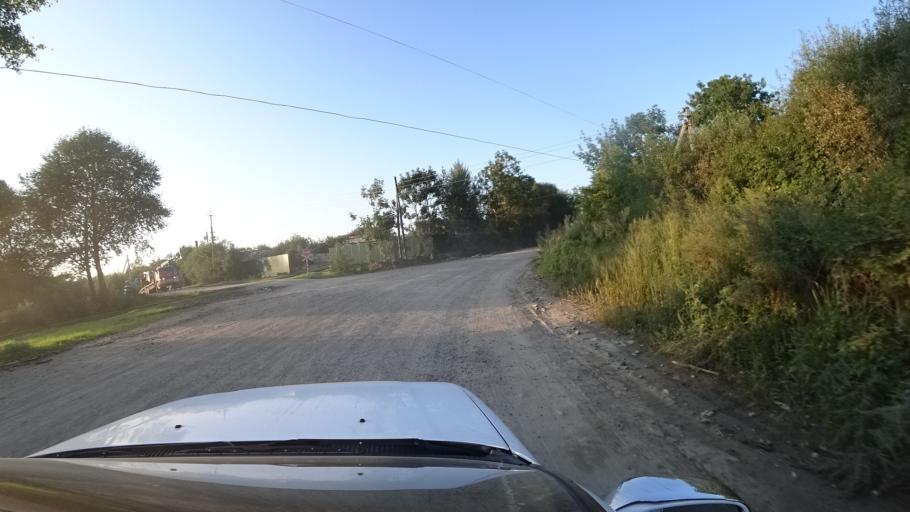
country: RU
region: Primorskiy
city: Dal'nerechensk
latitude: 45.9342
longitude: 133.7580
